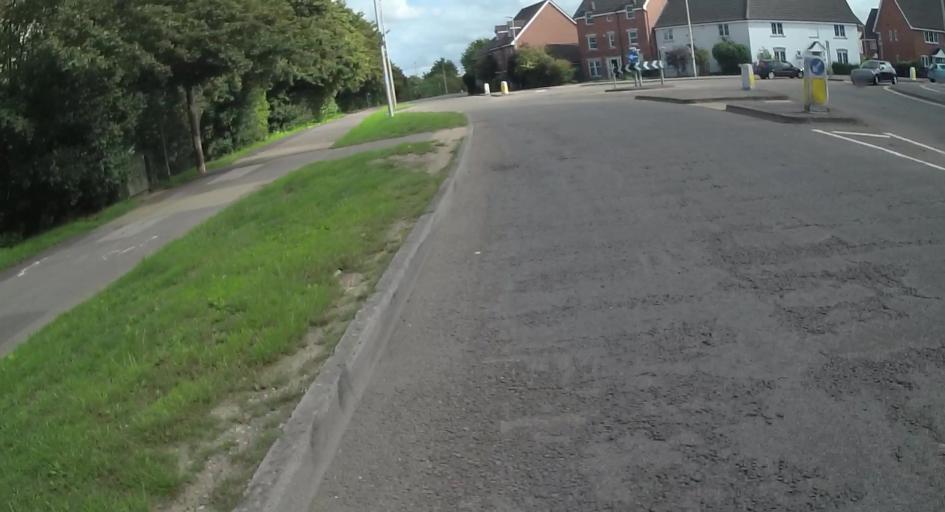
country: GB
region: England
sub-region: West Berkshire
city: Thatcham
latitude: 51.3957
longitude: -1.2468
